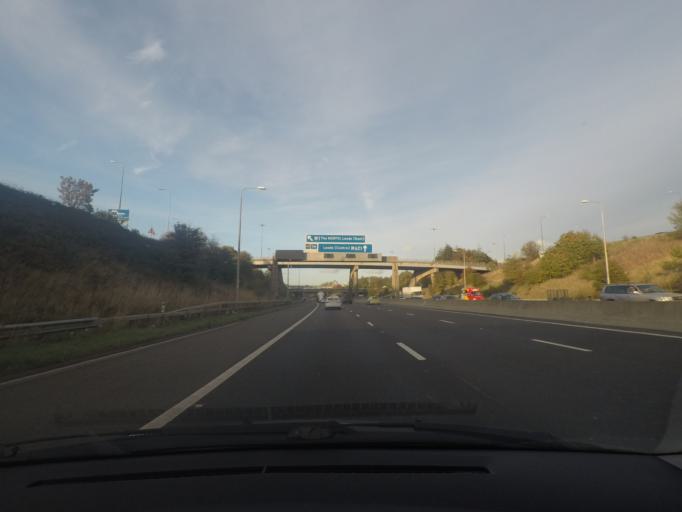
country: GB
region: England
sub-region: City and Borough of Leeds
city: Lofthouse
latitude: 53.7288
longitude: -1.5133
